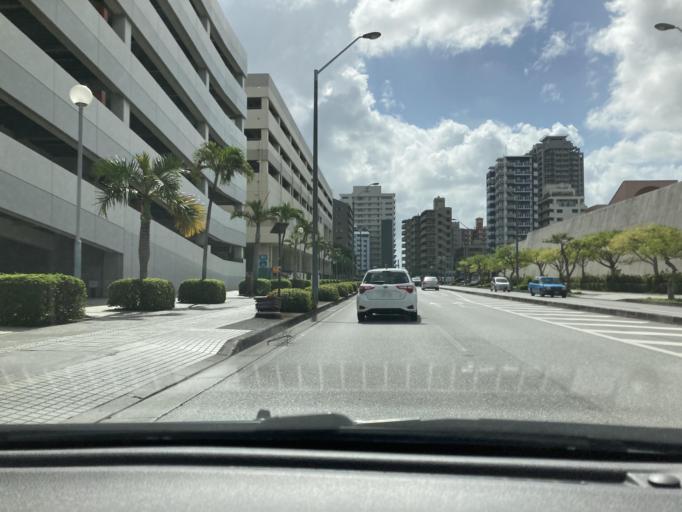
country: JP
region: Okinawa
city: Naha-shi
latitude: 26.2269
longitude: 127.6950
